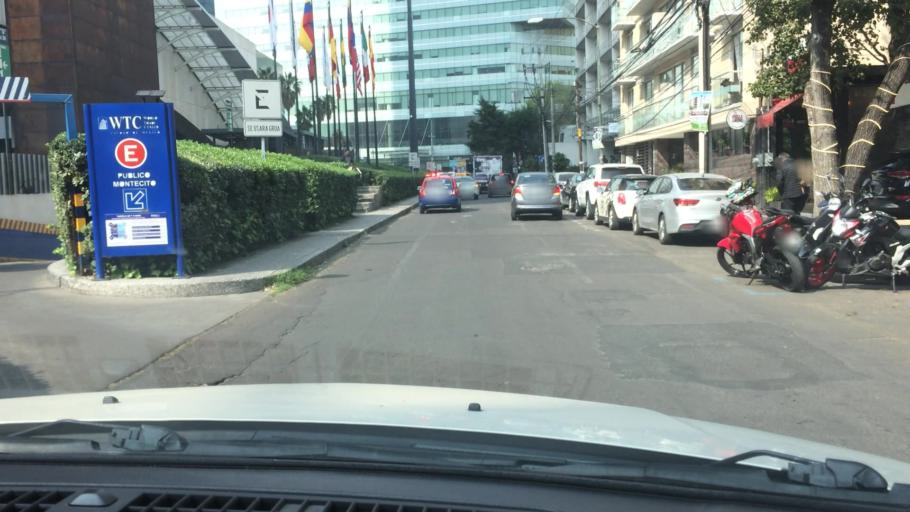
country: MX
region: Mexico City
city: Colonia del Valle
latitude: 19.3949
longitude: -99.1731
